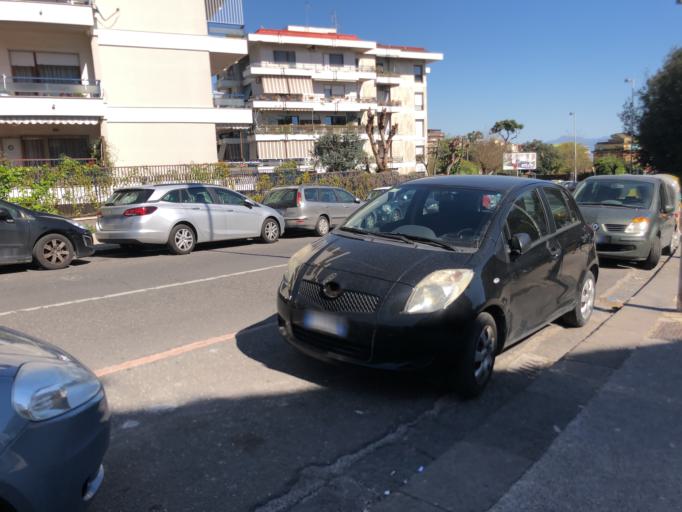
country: IT
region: Campania
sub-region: Provincia di Napoli
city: Napoli
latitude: 40.8590
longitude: 14.2242
